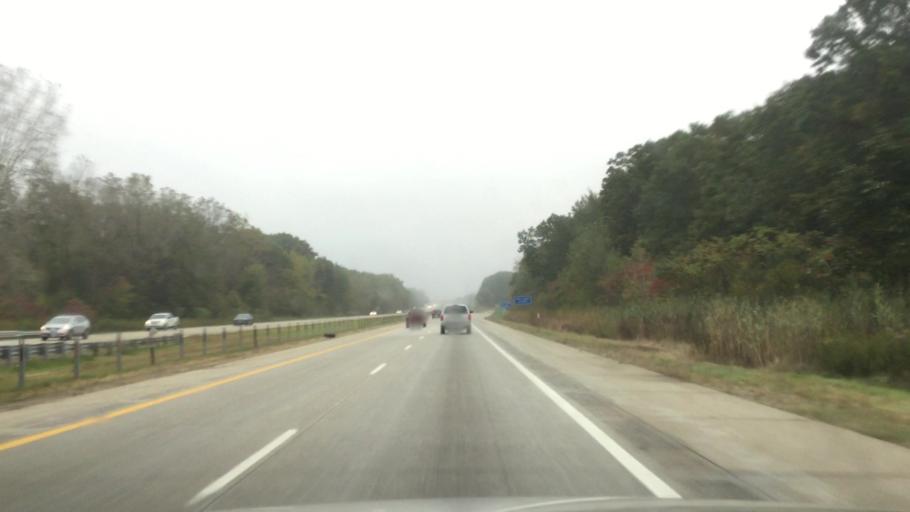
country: US
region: Michigan
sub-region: Berrien County
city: Coloma
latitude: 42.1475
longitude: -86.3495
